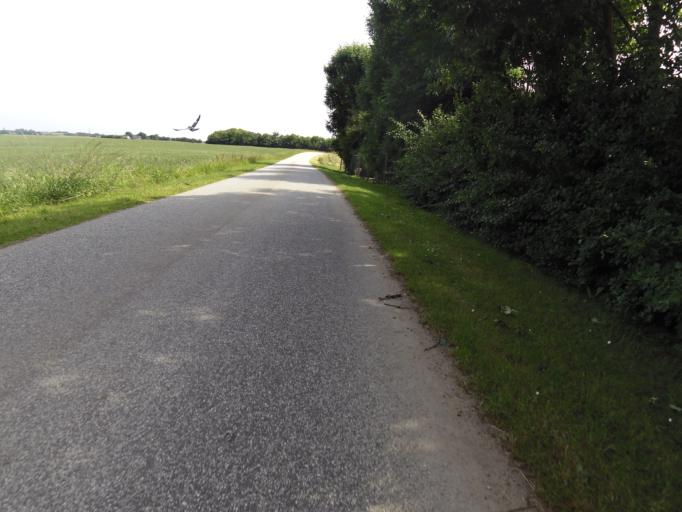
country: DK
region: Central Jutland
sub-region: Holstebro Kommune
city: Holstebro
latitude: 56.4284
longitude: 8.6546
